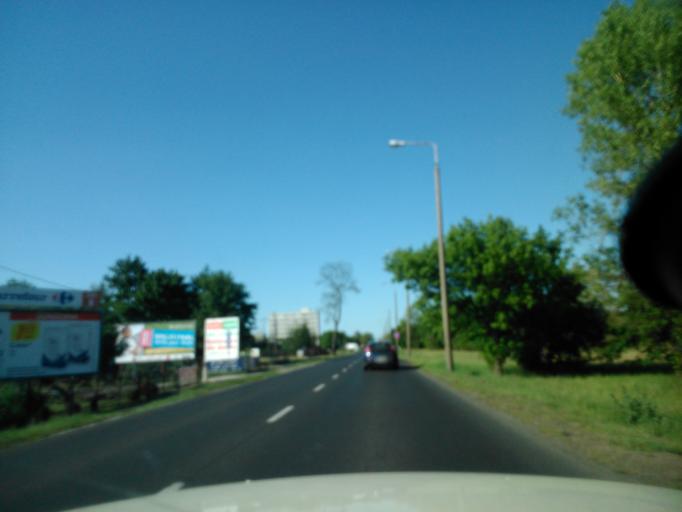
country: PL
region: Kujawsko-Pomorskie
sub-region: Torun
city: Torun
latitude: 52.9830
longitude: 18.5756
